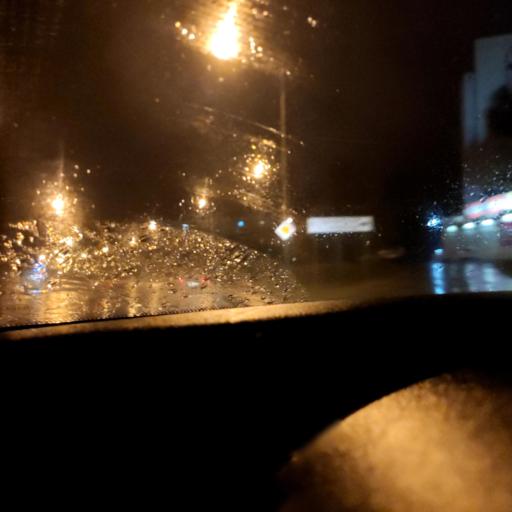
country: RU
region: Samara
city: Volzhskiy
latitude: 53.3535
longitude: 50.2117
